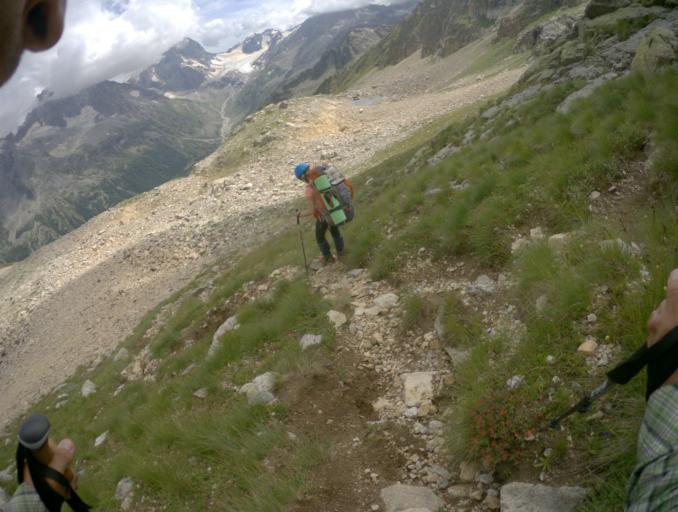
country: RU
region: Karachayevo-Cherkesiya
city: Uchkulan
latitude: 43.2752
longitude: 42.1224
